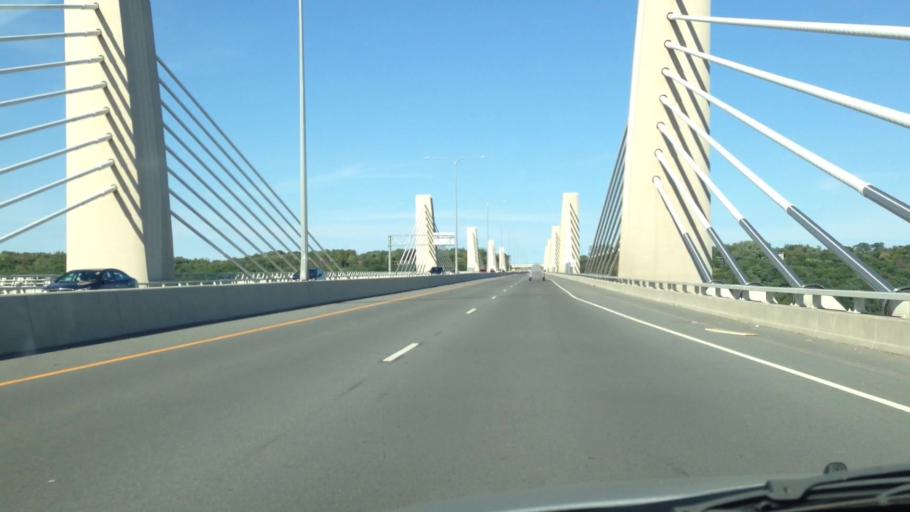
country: US
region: Minnesota
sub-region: Washington County
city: Oak Park Heights
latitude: 45.0388
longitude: -92.7877
